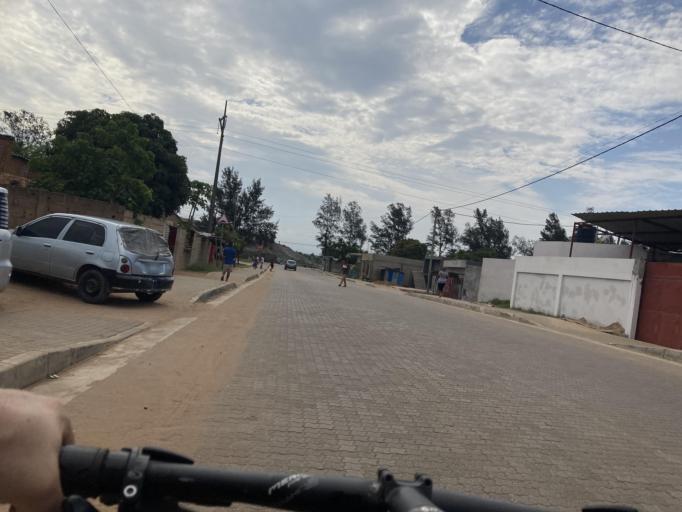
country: MZ
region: Maputo City
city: Maputo
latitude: -25.8995
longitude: 32.6010
